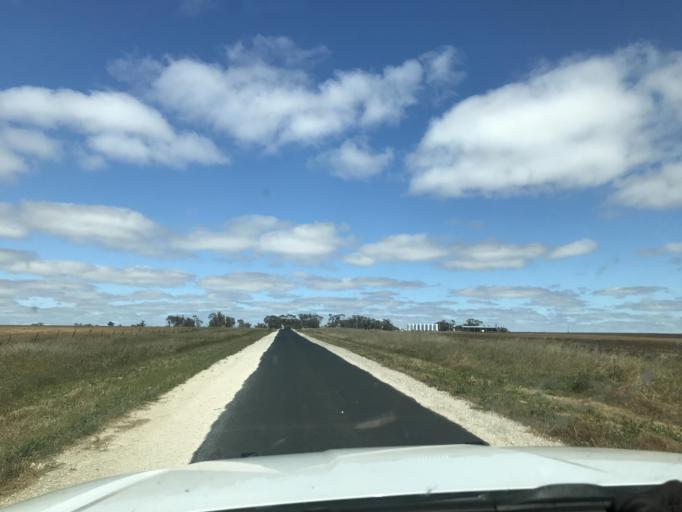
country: AU
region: South Australia
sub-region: Tatiara
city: Bordertown
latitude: -36.3060
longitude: 141.0841
